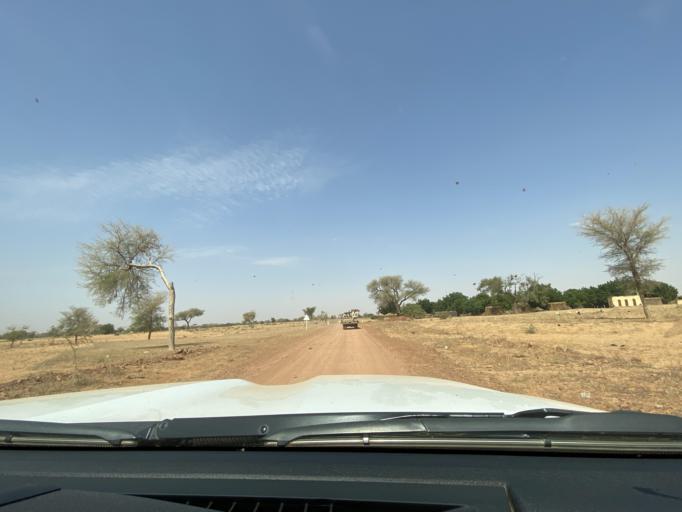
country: NE
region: Dosso
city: Birnin Gaoure
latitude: 13.2416
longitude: 2.8663
